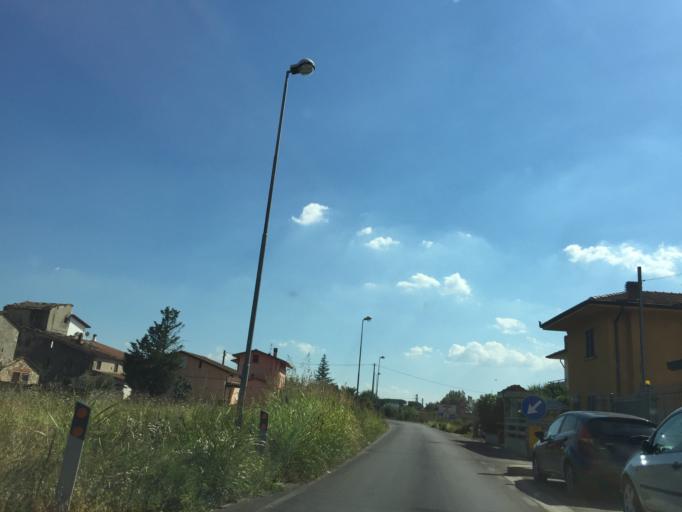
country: IT
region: Tuscany
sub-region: Provincia di Pistoia
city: Monsummano Terme
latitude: 43.8574
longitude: 10.8047
